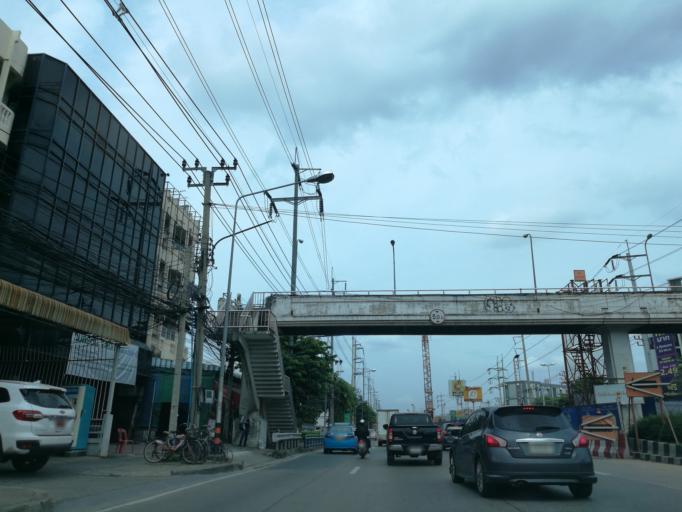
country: TH
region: Bangkok
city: Bang Khen
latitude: 13.8640
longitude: 100.6157
